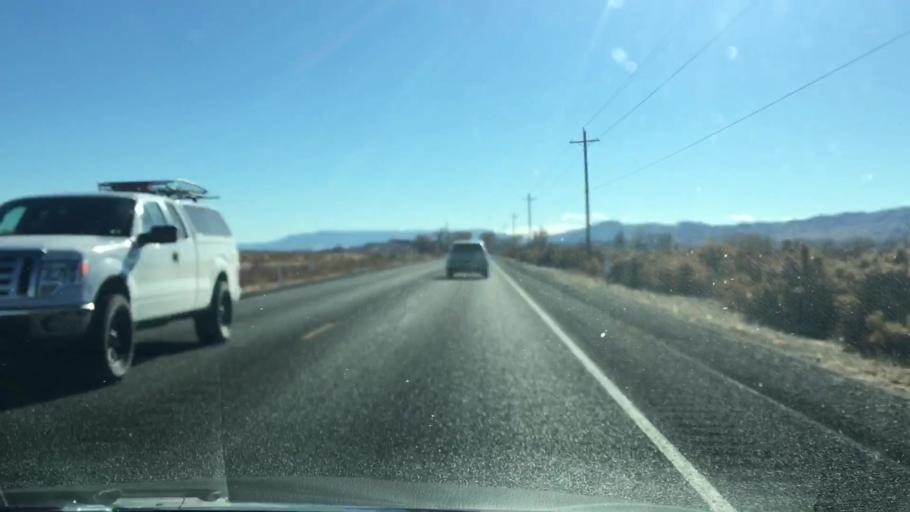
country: US
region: Nevada
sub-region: Lyon County
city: Yerington
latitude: 39.0573
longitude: -119.1814
